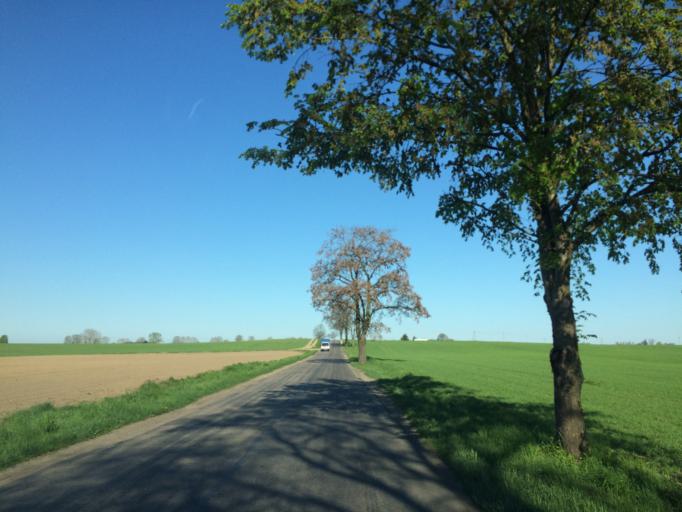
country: PL
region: Warmian-Masurian Voivodeship
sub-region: Powiat dzialdowski
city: Rybno
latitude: 53.3952
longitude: 19.8951
